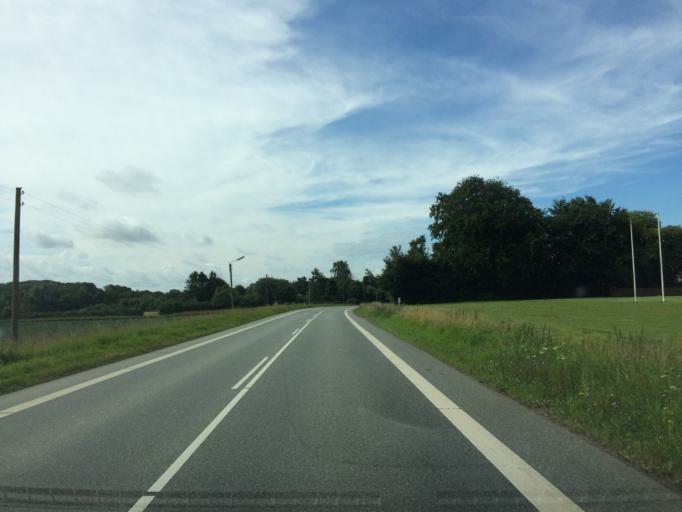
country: DK
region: South Denmark
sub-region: Odense Kommune
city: Bellinge
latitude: 55.3086
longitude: 10.3080
